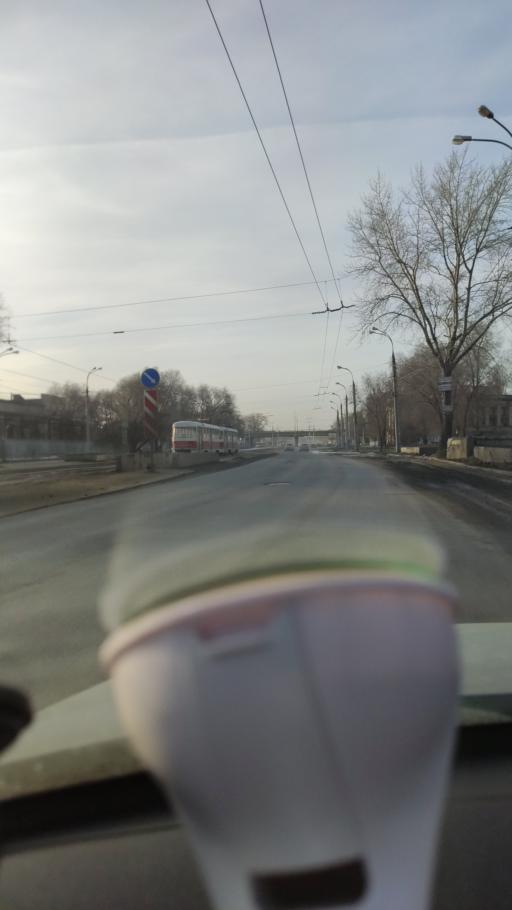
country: RU
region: Samara
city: Smyshlyayevka
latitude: 53.2062
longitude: 50.2786
